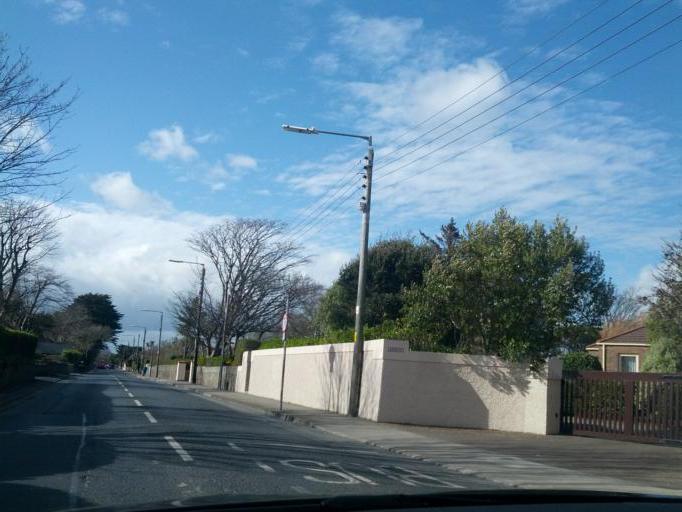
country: IE
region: Leinster
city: Sutton
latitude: 53.3877
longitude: -6.1058
